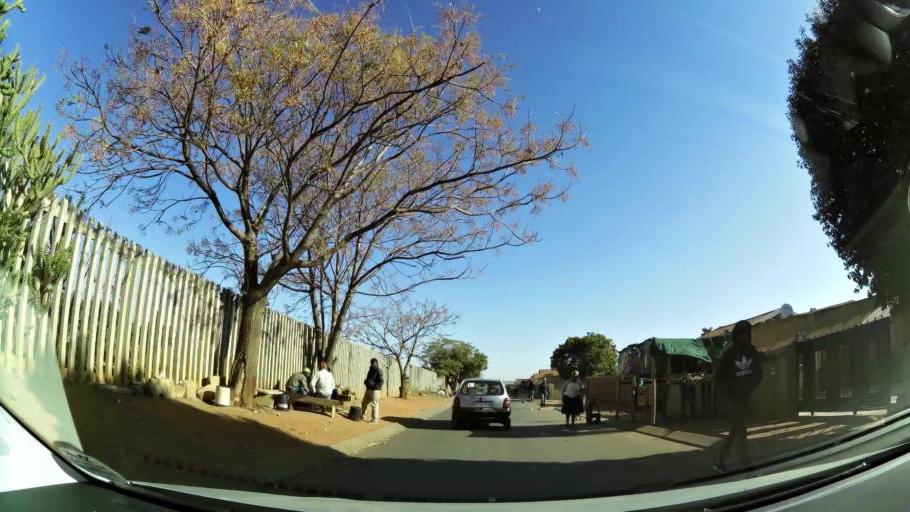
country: ZA
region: Gauteng
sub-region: Ekurhuleni Metropolitan Municipality
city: Tembisa
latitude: -26.0223
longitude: 28.2250
